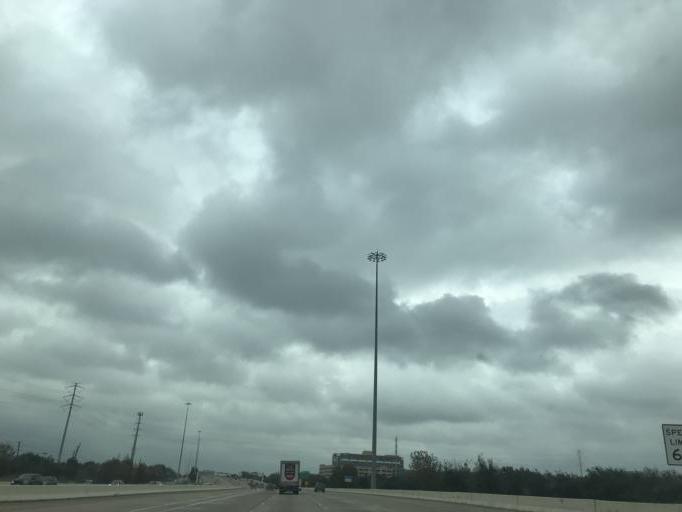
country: US
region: Texas
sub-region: Fort Bend County
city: Sugar Land
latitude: 29.5929
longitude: -95.6288
